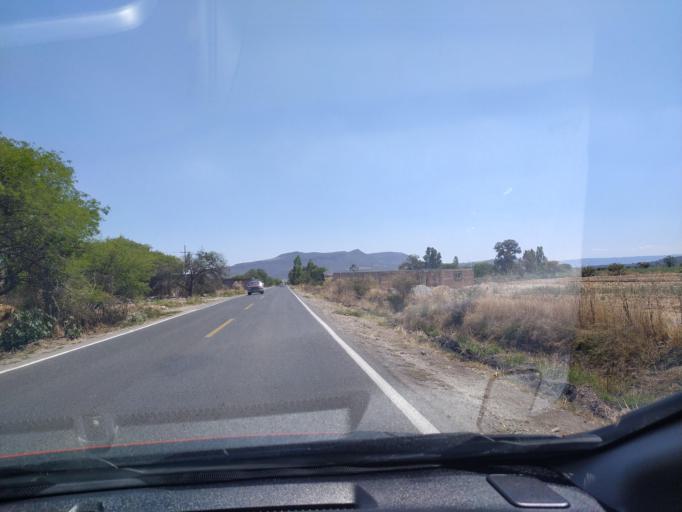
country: MX
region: Guanajuato
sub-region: San Francisco del Rincon
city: San Ignacio de Hidalgo
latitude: 20.8546
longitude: -101.8575
